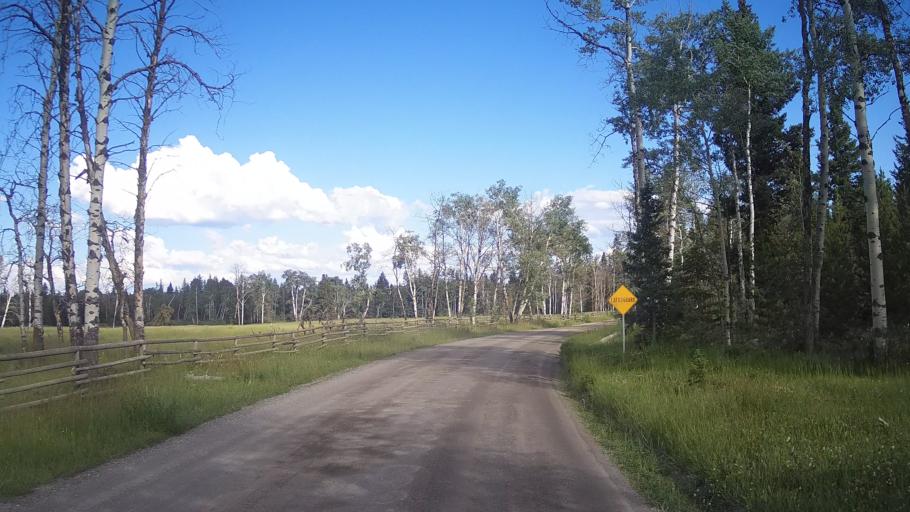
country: CA
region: British Columbia
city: Cache Creek
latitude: 51.1796
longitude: -121.5784
